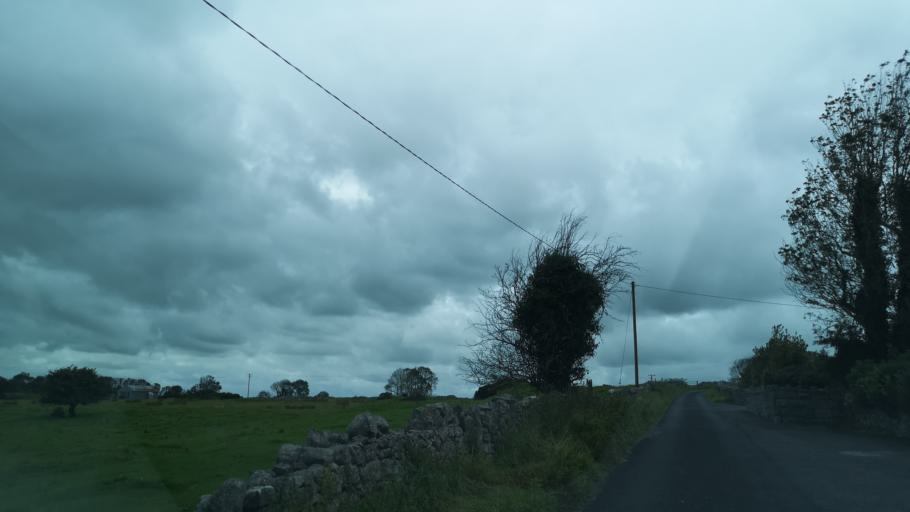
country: IE
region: Connaught
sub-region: County Galway
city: Athenry
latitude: 53.3106
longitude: -8.7429
